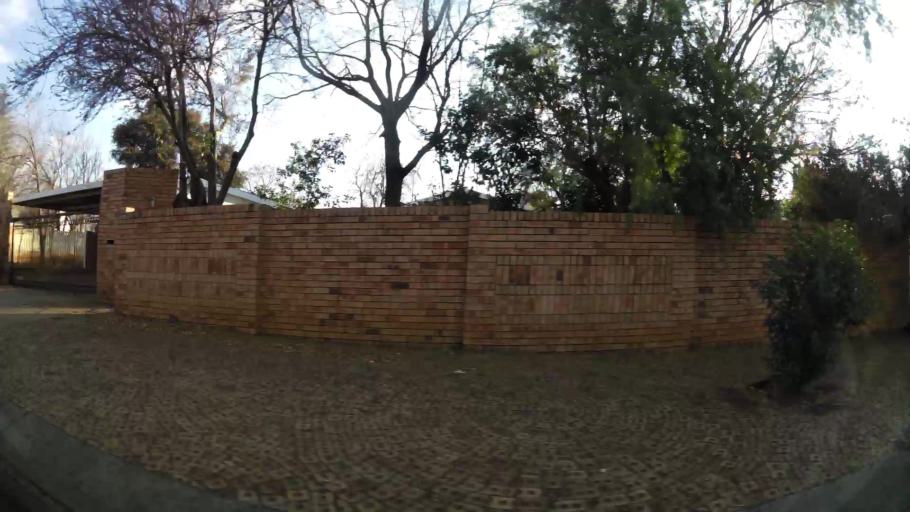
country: ZA
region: Orange Free State
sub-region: Mangaung Metropolitan Municipality
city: Bloemfontein
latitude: -29.1486
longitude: 26.1807
